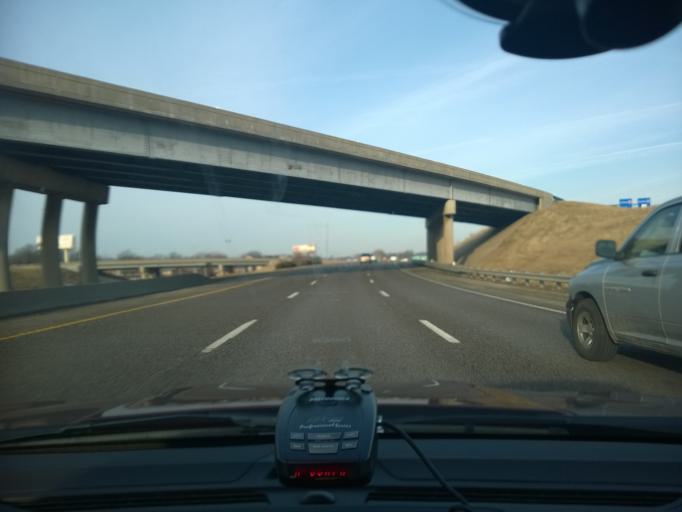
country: US
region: Missouri
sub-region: Saint Louis County
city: Woodson Terrace
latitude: 38.7332
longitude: -90.3485
